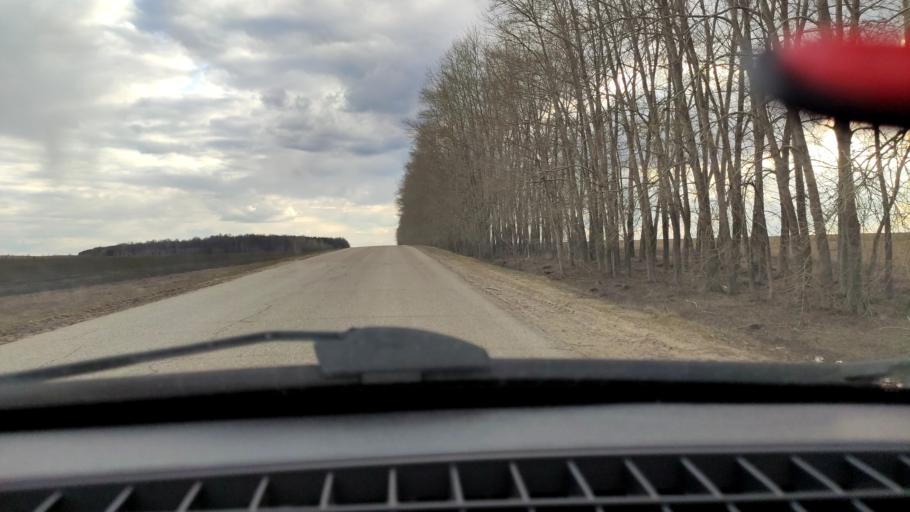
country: RU
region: Bashkortostan
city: Karmaskaly
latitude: 54.3065
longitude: 55.9374
